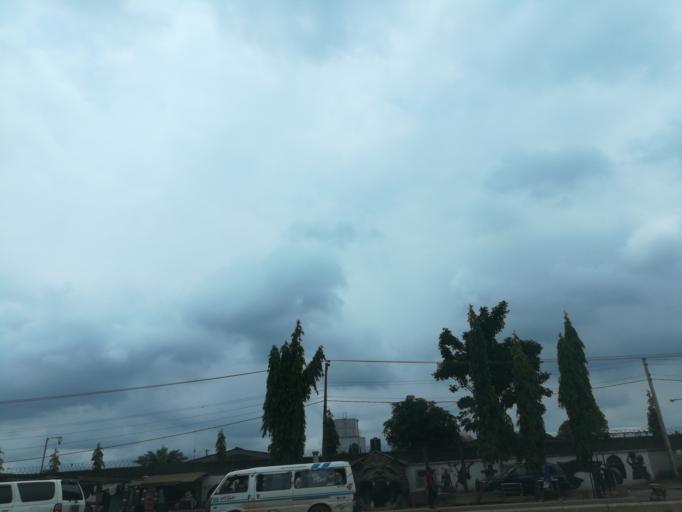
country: NG
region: Lagos
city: Ikeja
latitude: 6.5944
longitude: 3.3361
